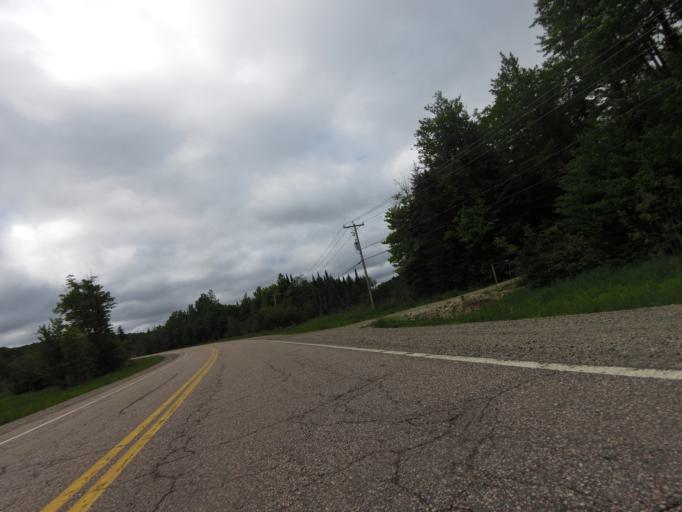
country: CA
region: Quebec
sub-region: Outaouais
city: Shawville
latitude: 45.8166
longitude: -76.4607
